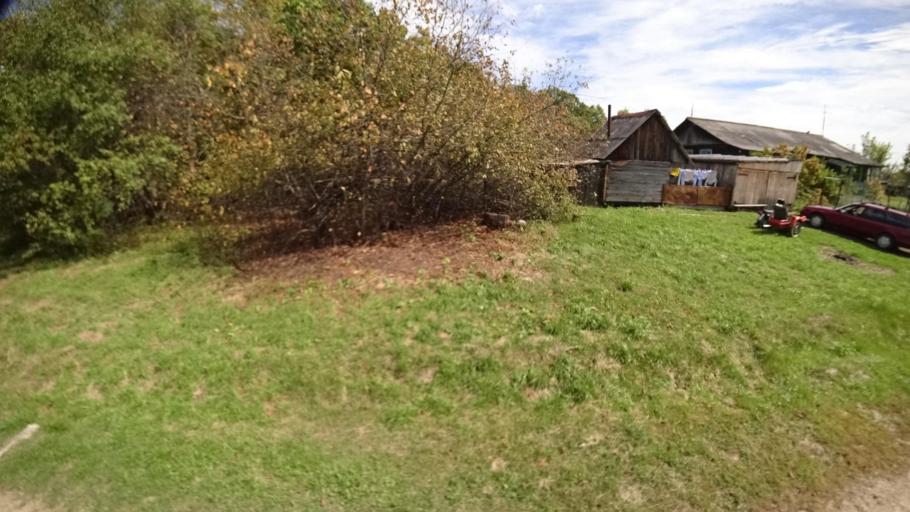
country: RU
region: Primorskiy
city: Yakovlevka
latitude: 44.6491
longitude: 133.5880
